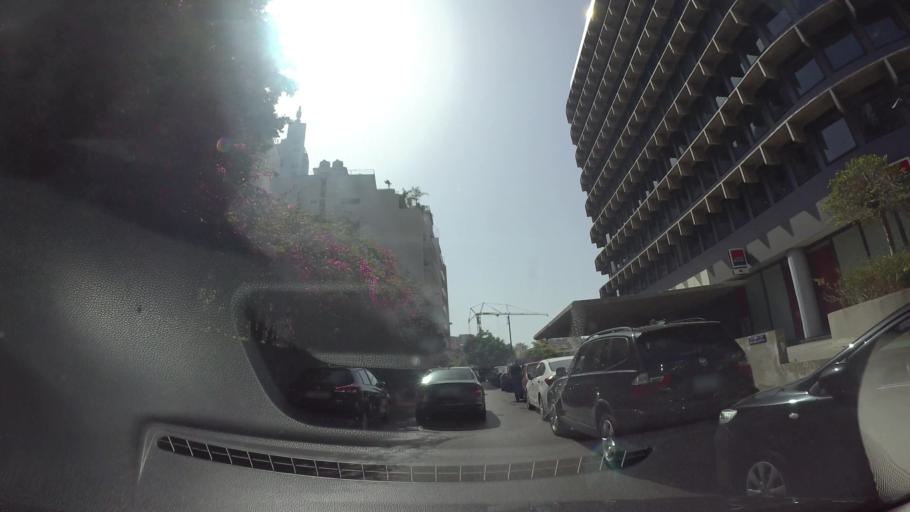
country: LB
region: Beyrouth
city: Beirut
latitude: 33.8989
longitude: 35.4954
